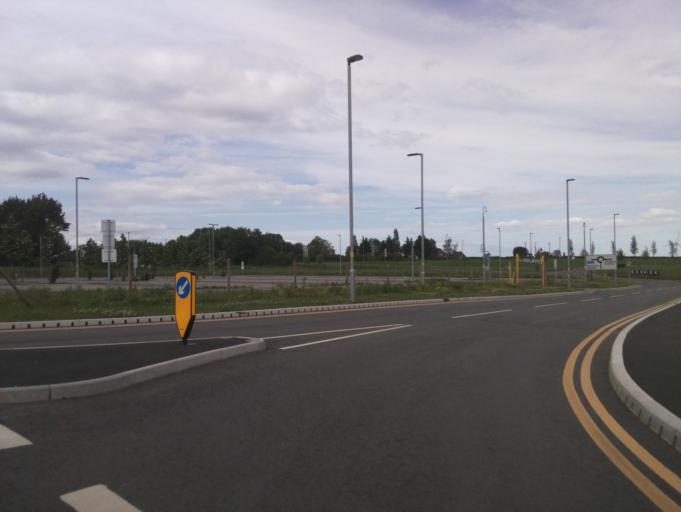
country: GB
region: England
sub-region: Worcestershire
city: Kempsey
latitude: 52.1570
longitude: -2.1578
